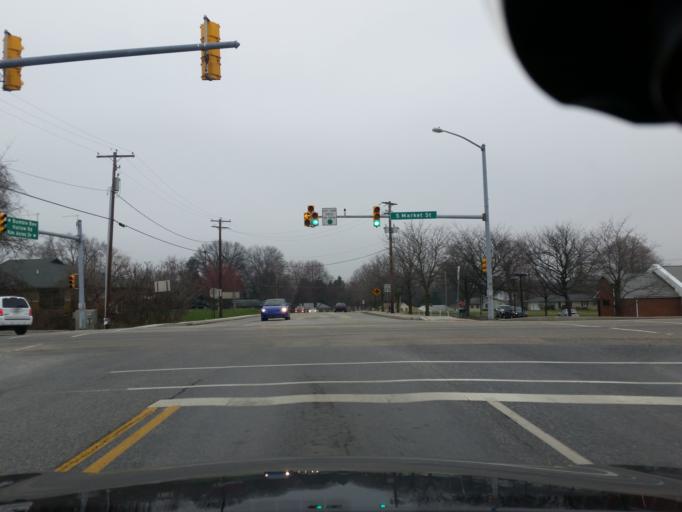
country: US
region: Pennsylvania
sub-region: Cumberland County
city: Mechanicsburg
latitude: 40.1761
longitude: -76.9850
